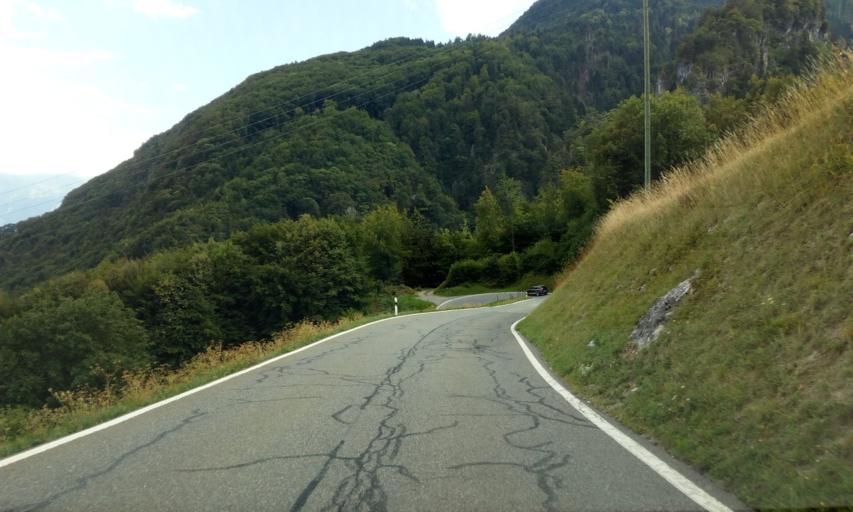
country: CH
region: Valais
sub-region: Monthey District
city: Vionnaz
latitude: 46.3080
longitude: 6.8914
